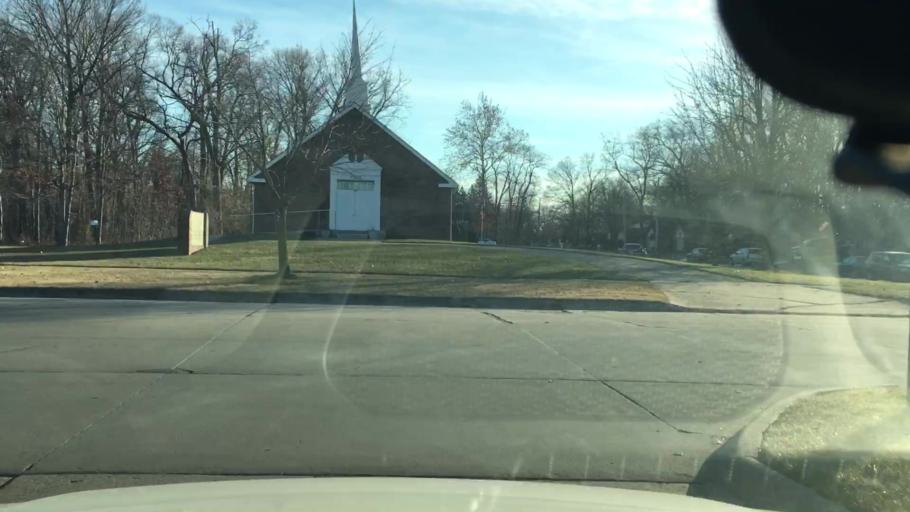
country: US
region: Michigan
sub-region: Oakland County
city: Madison Heights
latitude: 42.4983
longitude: -83.0770
